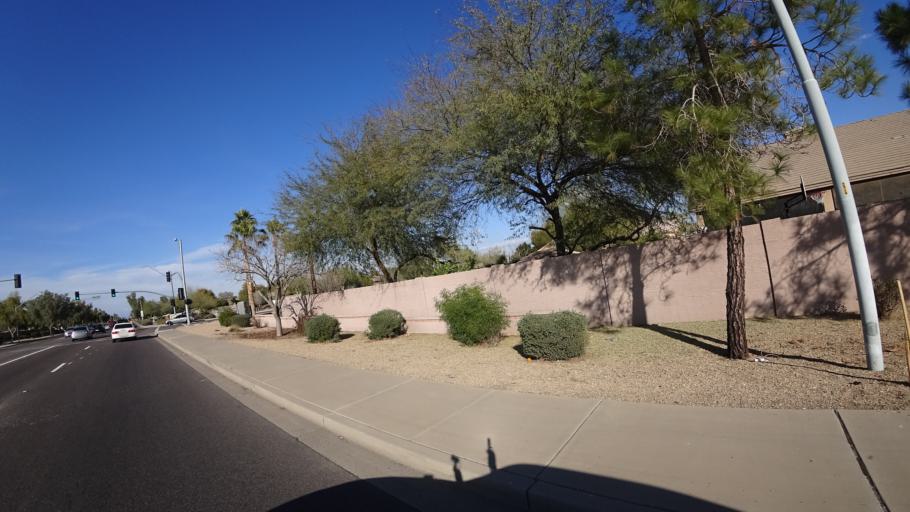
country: US
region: Arizona
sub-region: Maricopa County
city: Glendale
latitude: 33.5155
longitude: -112.2376
